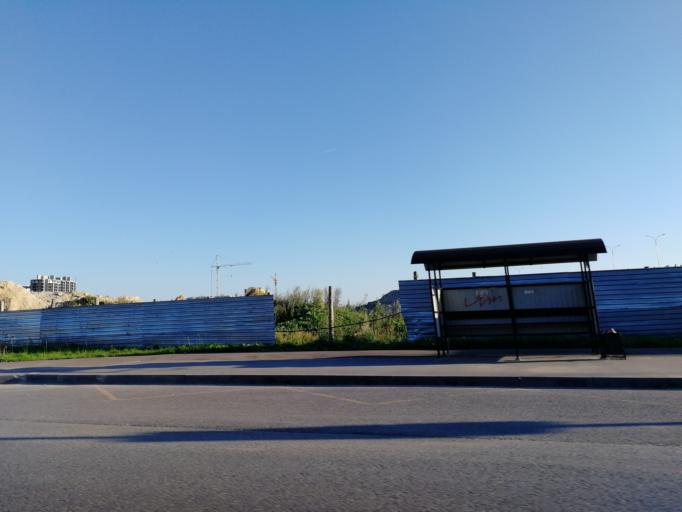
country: RU
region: Kaluga
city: Mstikhino
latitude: 54.4952
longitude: 36.1853
